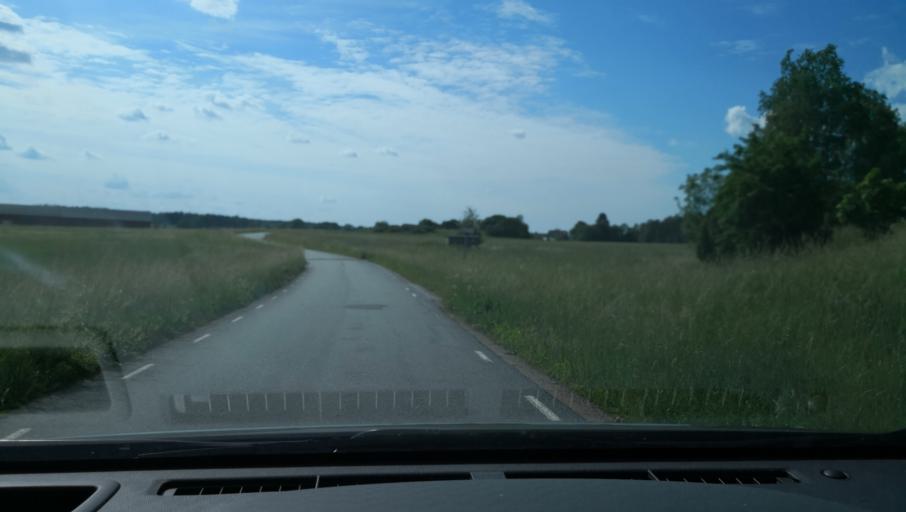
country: SE
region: Uppsala
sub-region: Enkopings Kommun
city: Orsundsbro
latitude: 59.8156
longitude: 17.3432
